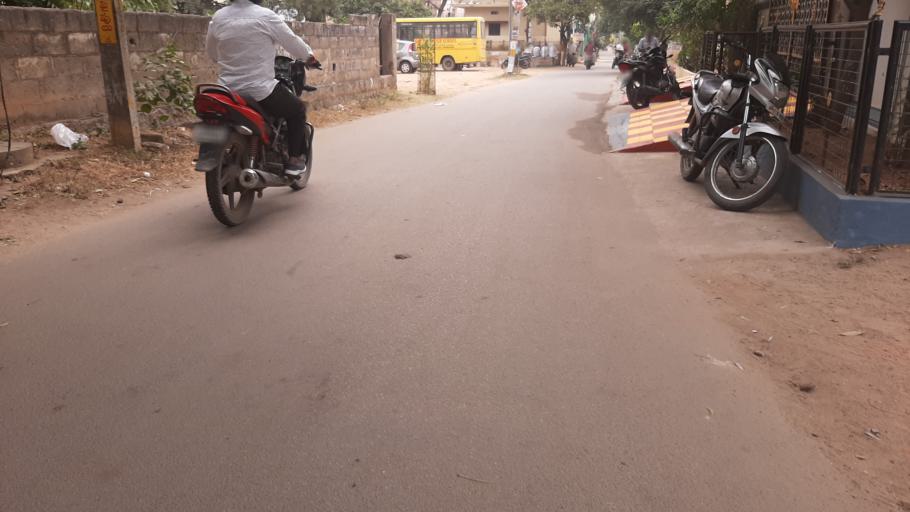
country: IN
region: Telangana
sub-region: Rangareddi
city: Lal Bahadur Nagar
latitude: 17.3474
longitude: 78.5557
